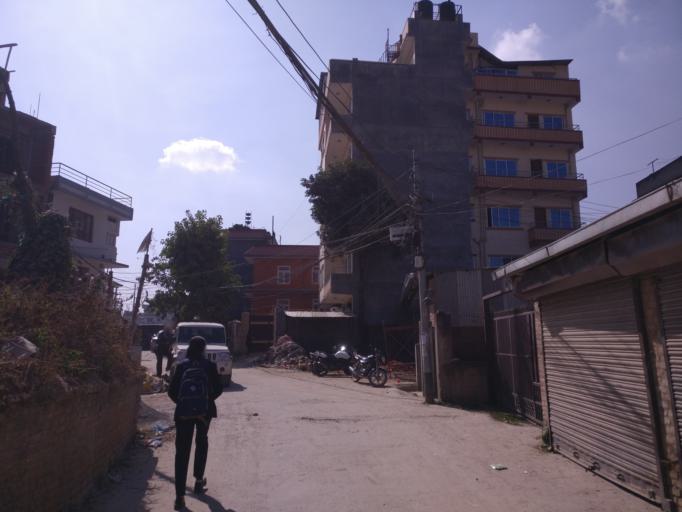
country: NP
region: Central Region
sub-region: Bagmati Zone
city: Patan
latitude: 27.6602
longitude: 85.3211
